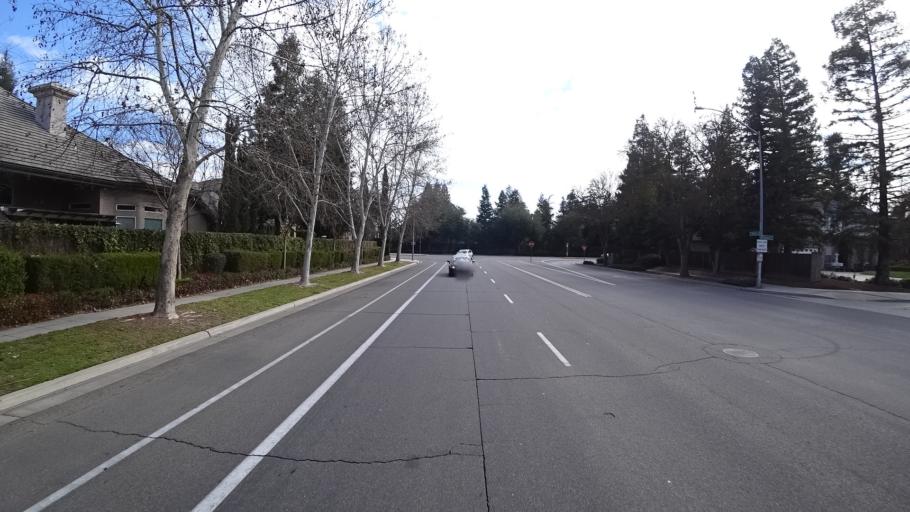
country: US
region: California
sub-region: Fresno County
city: West Park
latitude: 36.8443
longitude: -119.8801
